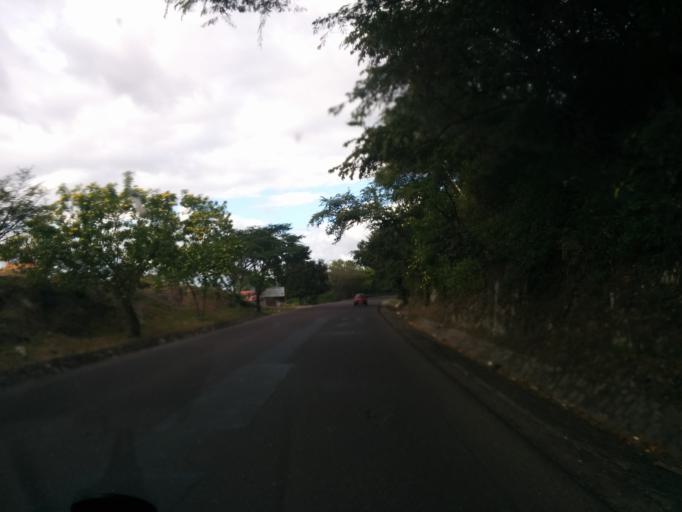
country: NI
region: Esteli
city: Esteli
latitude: 13.1550
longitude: -86.3702
